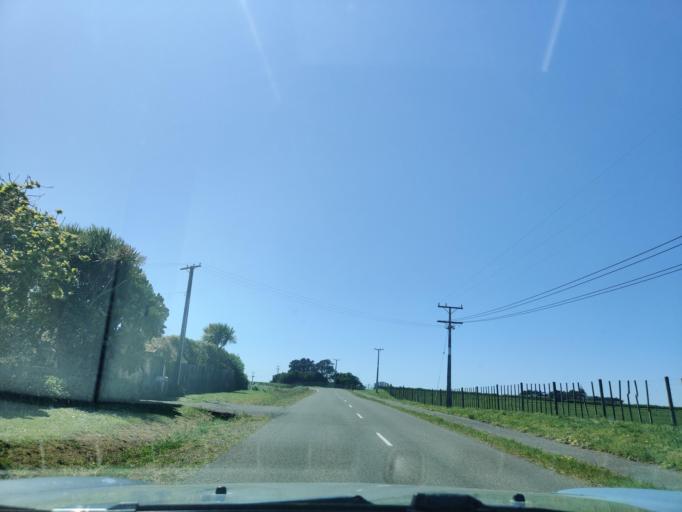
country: NZ
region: Taranaki
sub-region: South Taranaki District
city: Hawera
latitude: -39.5981
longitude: 174.2654
